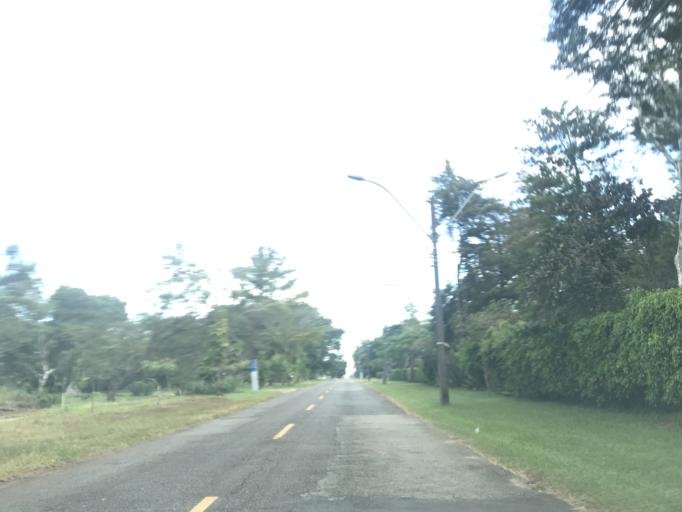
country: BR
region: Federal District
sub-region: Brasilia
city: Brasilia
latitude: -15.9031
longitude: -47.9394
